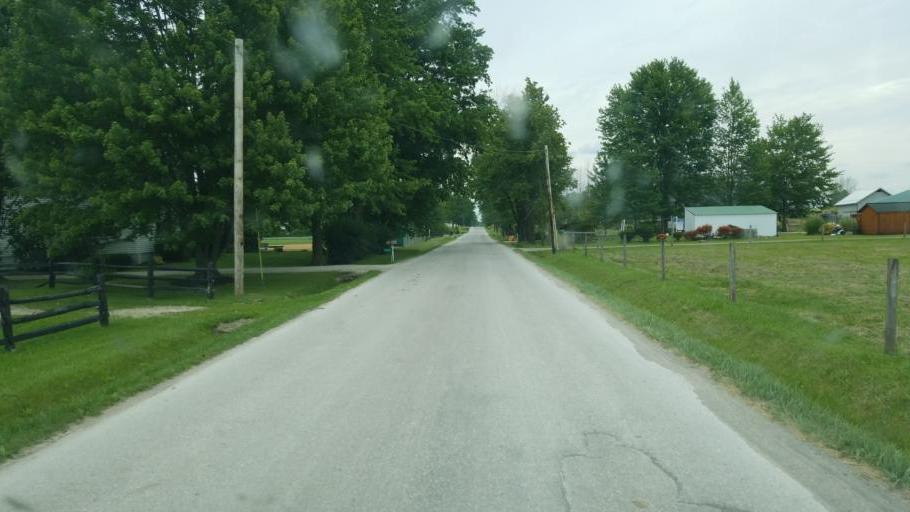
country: US
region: Ohio
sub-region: Geauga County
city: Middlefield
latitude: 41.4939
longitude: -81.0134
